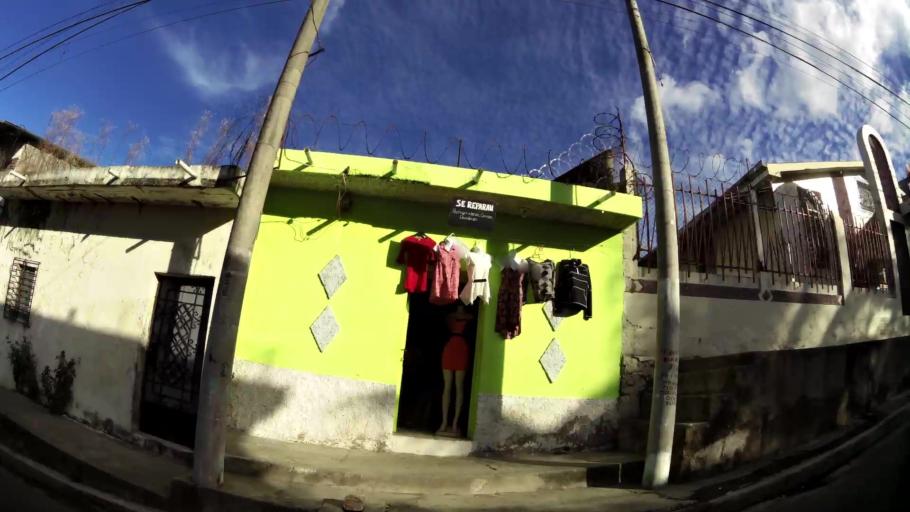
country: SV
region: Cuscatlan
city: Cojutepeque
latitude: 13.7224
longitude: -88.9384
